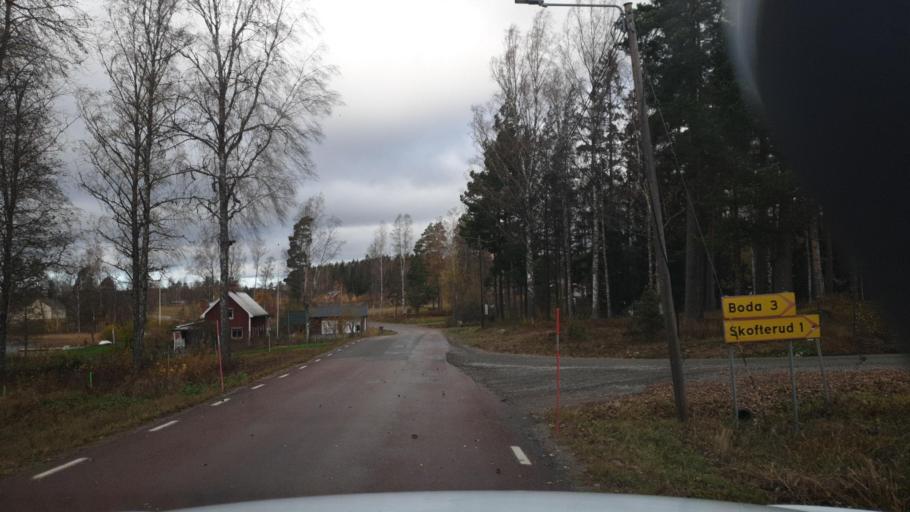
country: SE
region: Vaermland
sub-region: Arvika Kommun
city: Arvika
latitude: 59.5342
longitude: 12.8157
